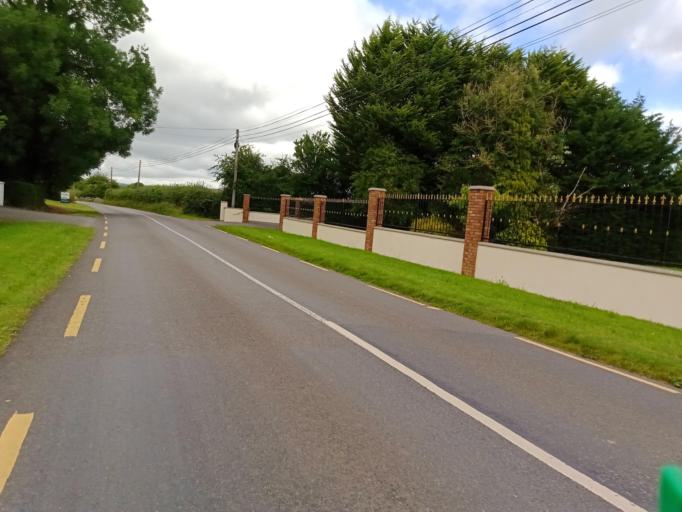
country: IE
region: Leinster
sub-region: Kilkenny
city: Callan
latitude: 52.5581
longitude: -7.4095
